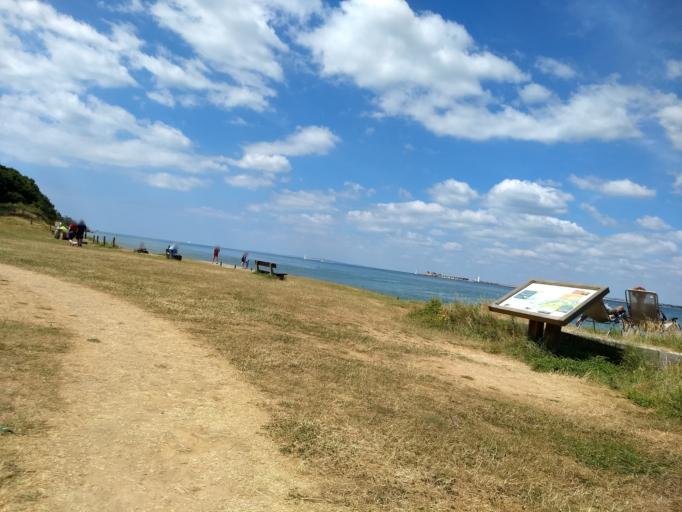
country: GB
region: England
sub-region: Isle of Wight
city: Freshwater
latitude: 50.7070
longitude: -1.5218
